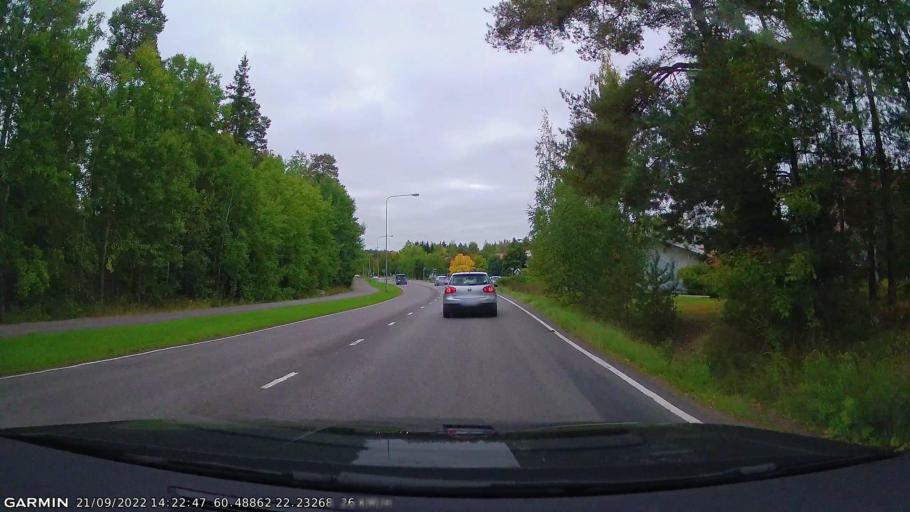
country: FI
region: Varsinais-Suomi
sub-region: Turku
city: Rusko
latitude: 60.4889
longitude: 22.2327
